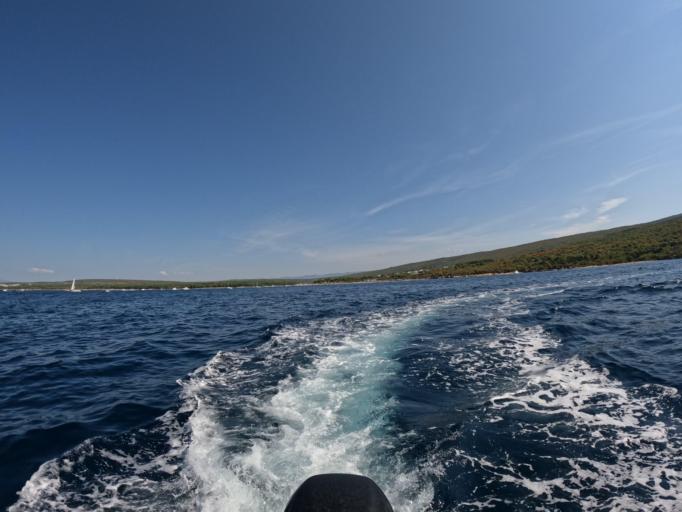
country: HR
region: Primorsko-Goranska
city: Punat
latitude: 45.0015
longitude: 14.6202
